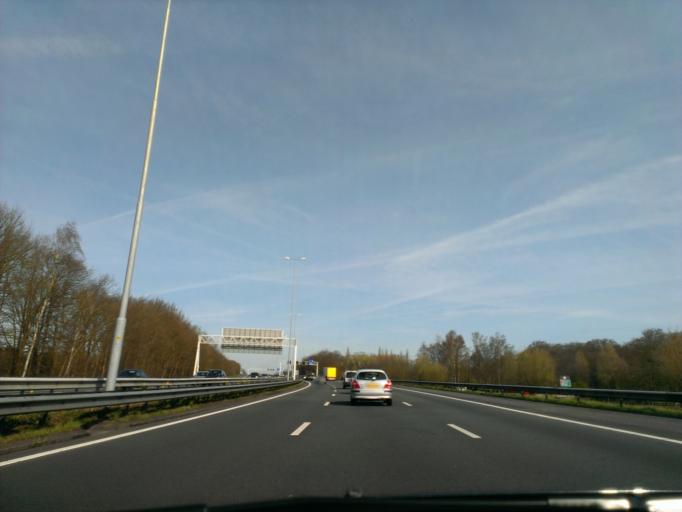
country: NL
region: North Holland
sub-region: Gemeente Naarden
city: Naarden
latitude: 52.2880
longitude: 5.1833
